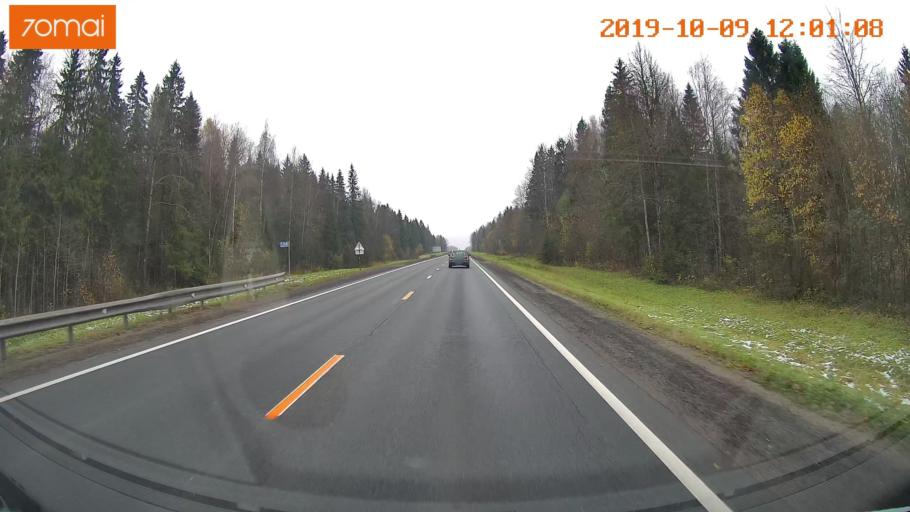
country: RU
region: Vologda
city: Gryazovets
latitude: 58.6915
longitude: 40.3020
